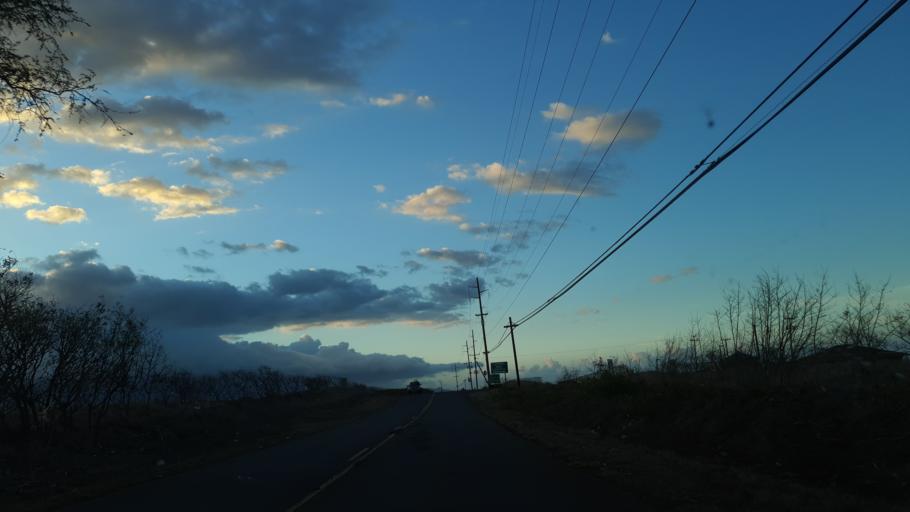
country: US
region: Hawaii
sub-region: Maui County
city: Kahului
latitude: 20.8575
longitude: -156.4238
